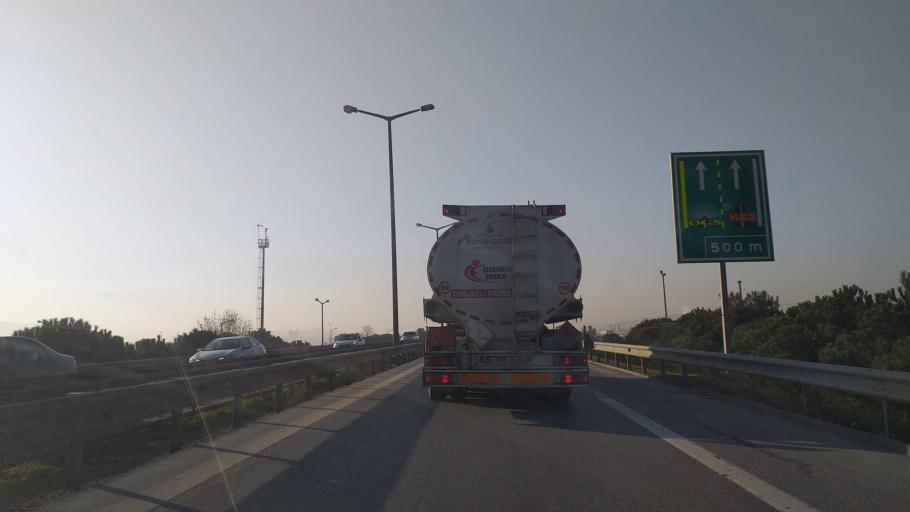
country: TR
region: Istanbul
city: Samandira
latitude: 40.9835
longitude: 29.2060
